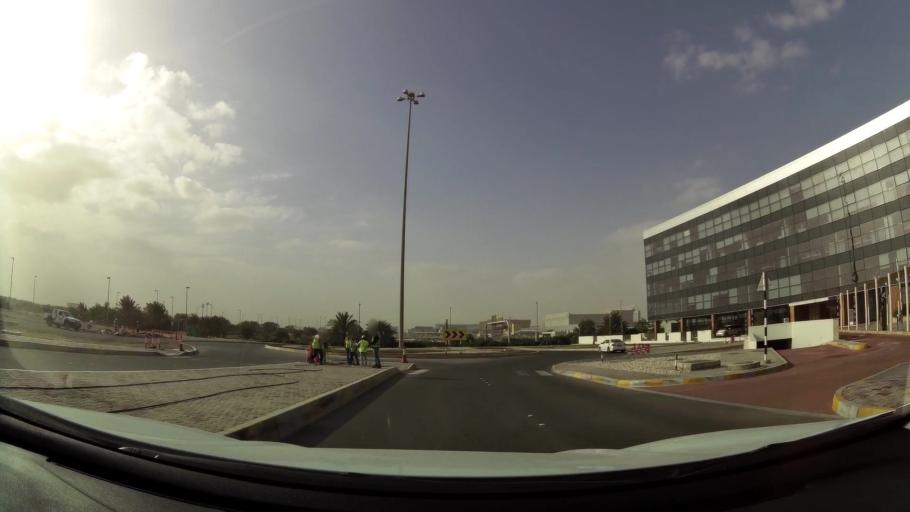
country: AE
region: Abu Dhabi
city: Abu Dhabi
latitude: 24.4286
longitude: 54.6407
